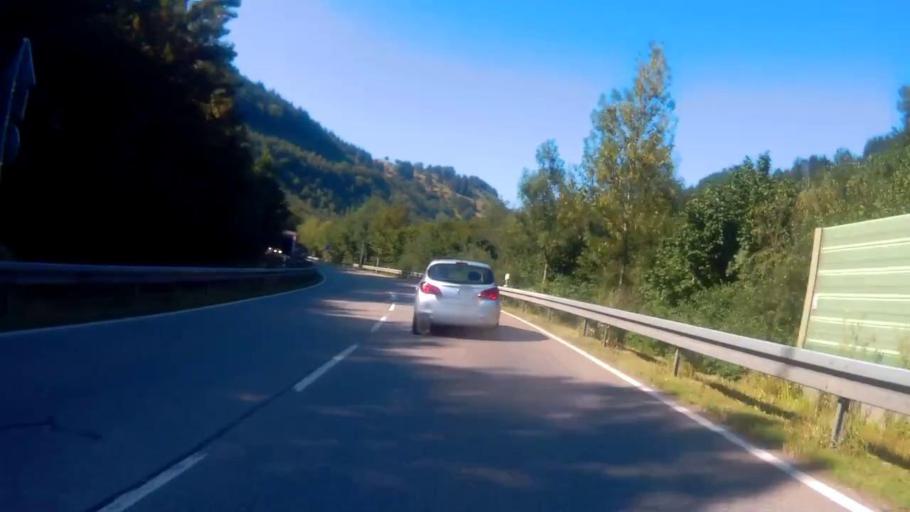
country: DE
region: Baden-Wuerttemberg
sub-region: Freiburg Region
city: Zell im Wiesental
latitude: 47.7116
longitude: 7.8626
